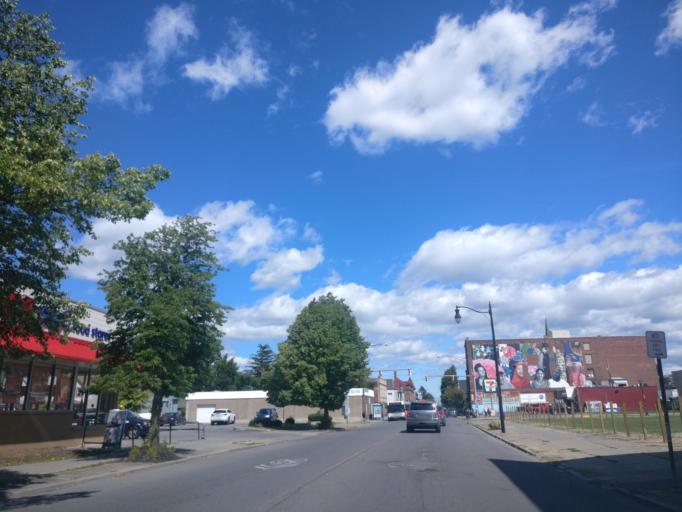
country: US
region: New York
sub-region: Erie County
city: Buffalo
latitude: 42.9178
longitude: -78.8907
